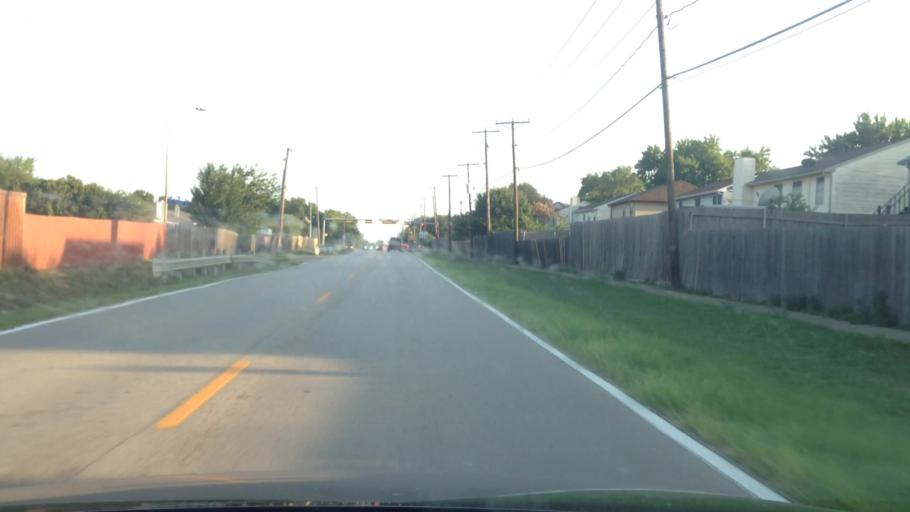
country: US
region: Texas
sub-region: Tarrant County
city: Dalworthington Gardens
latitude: 32.6466
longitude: -97.1023
